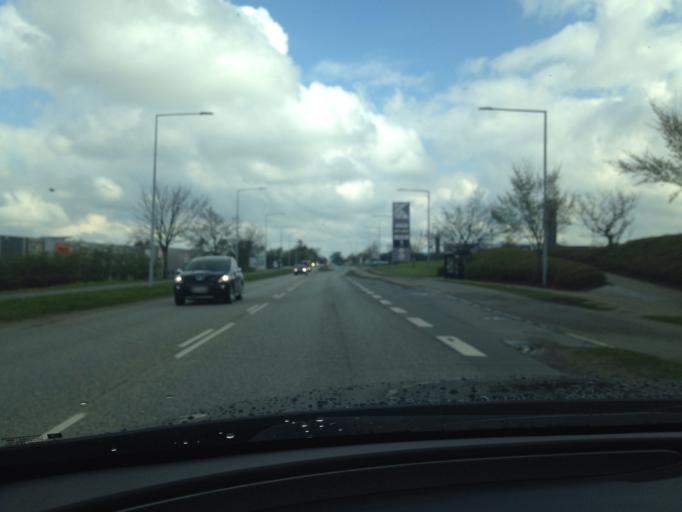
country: DK
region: South Denmark
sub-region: Kolding Kommune
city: Kolding
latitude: 55.5143
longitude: 9.4574
